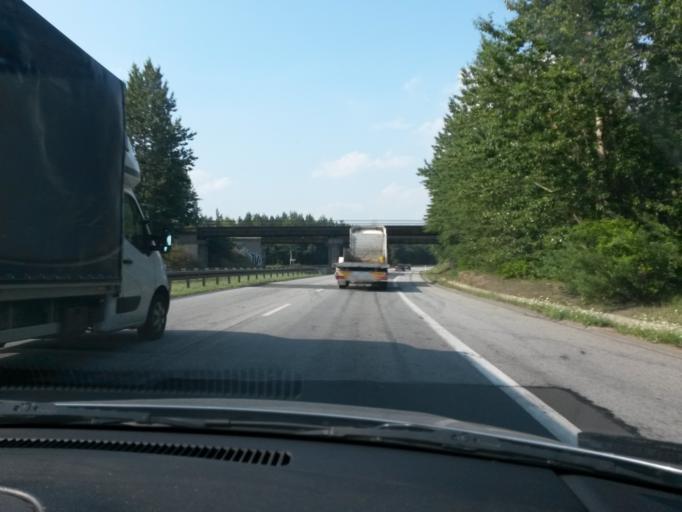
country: PL
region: Silesian Voivodeship
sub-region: Myslowice
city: Myslowice
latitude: 50.2295
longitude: 19.1676
